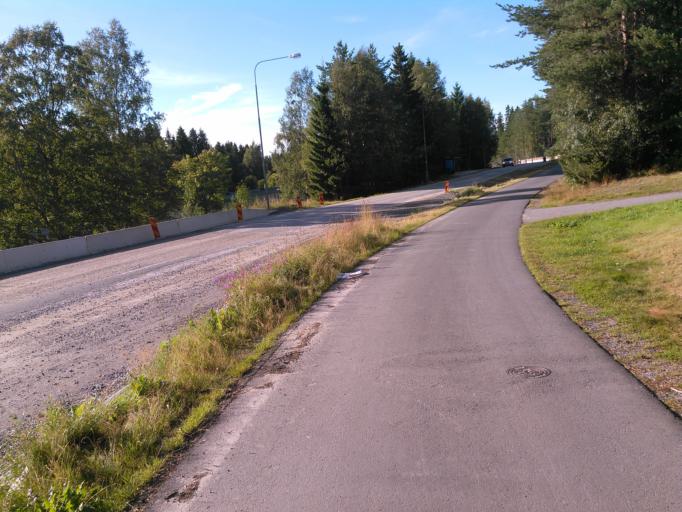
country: SE
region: Vaesterbotten
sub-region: Umea Kommun
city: Ersmark
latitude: 63.8275
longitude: 20.3248
